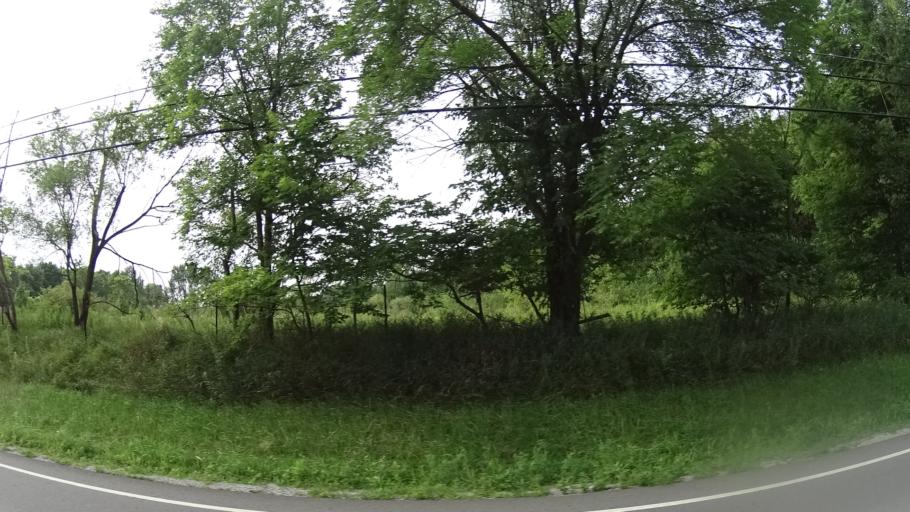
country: US
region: Indiana
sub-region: Madison County
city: Pendleton
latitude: 40.0032
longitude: -85.7598
